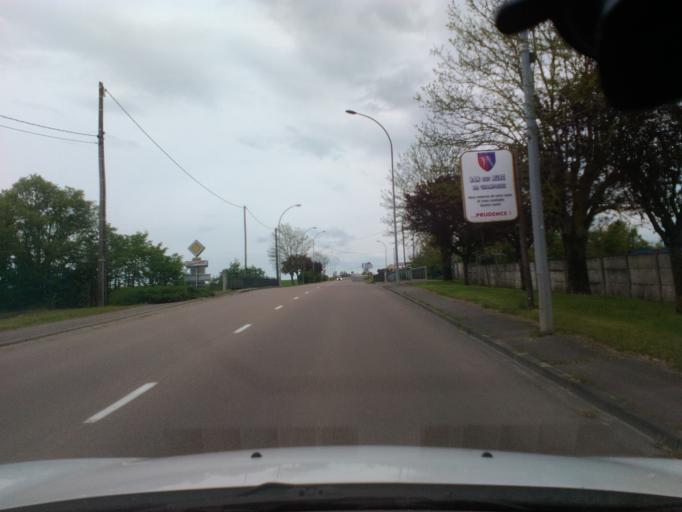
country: FR
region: Champagne-Ardenne
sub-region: Departement de l'Aube
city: Bar-sur-Aube
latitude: 48.2280
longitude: 4.7204
